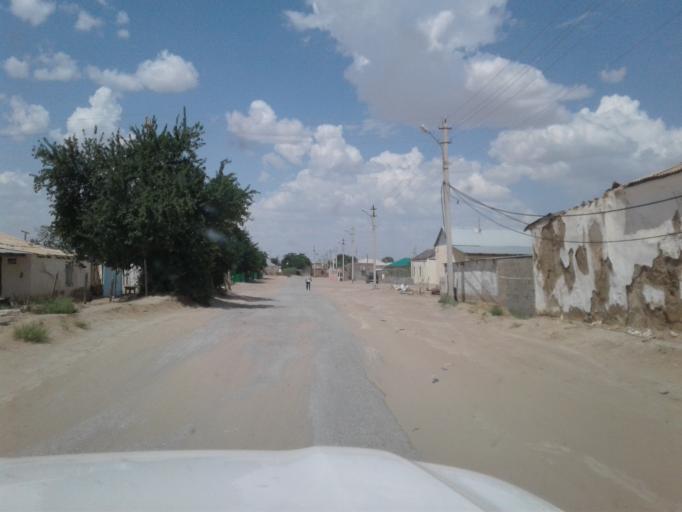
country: TM
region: Ahal
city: Abadan
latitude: 38.7628
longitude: 58.4934
